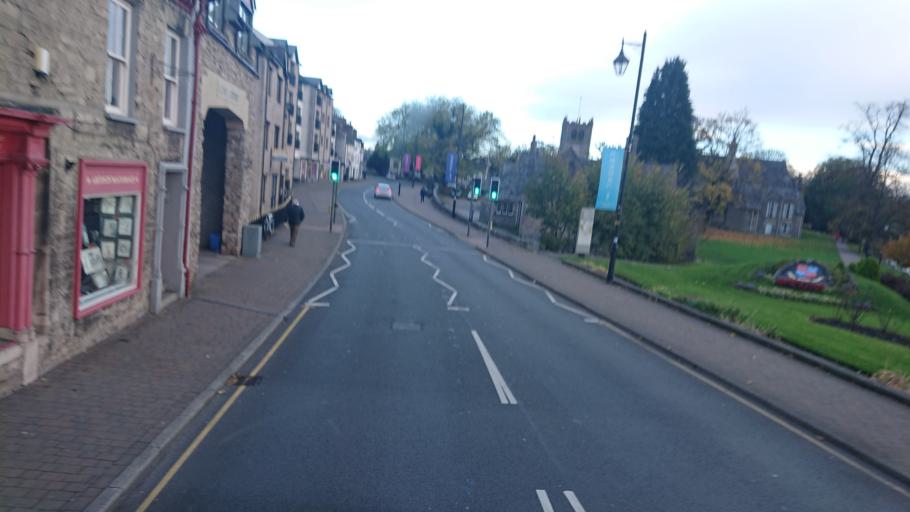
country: GB
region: England
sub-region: Cumbria
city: Kendal
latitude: 54.3209
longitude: -2.7451
